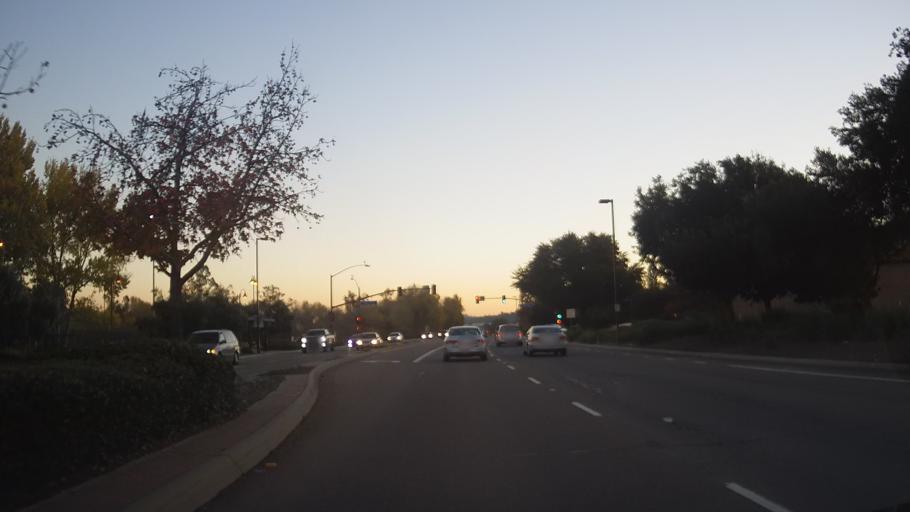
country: US
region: California
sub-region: San Diego County
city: Santee
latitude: 32.8488
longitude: -116.9835
